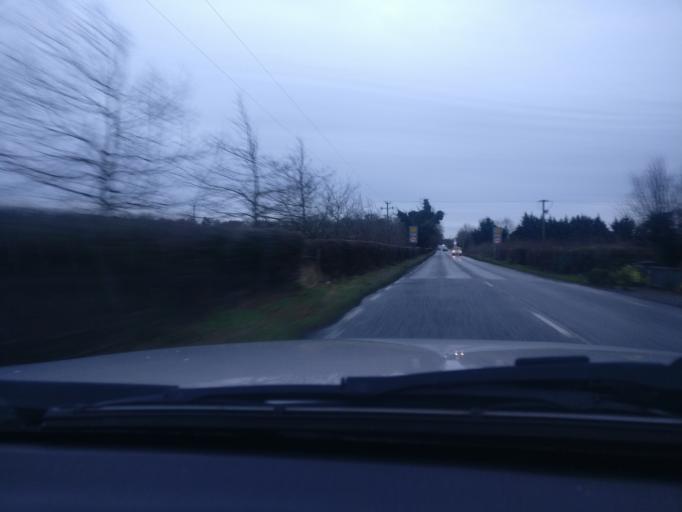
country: IE
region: Leinster
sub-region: An Mhi
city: Navan
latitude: 53.6742
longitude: -6.7431
